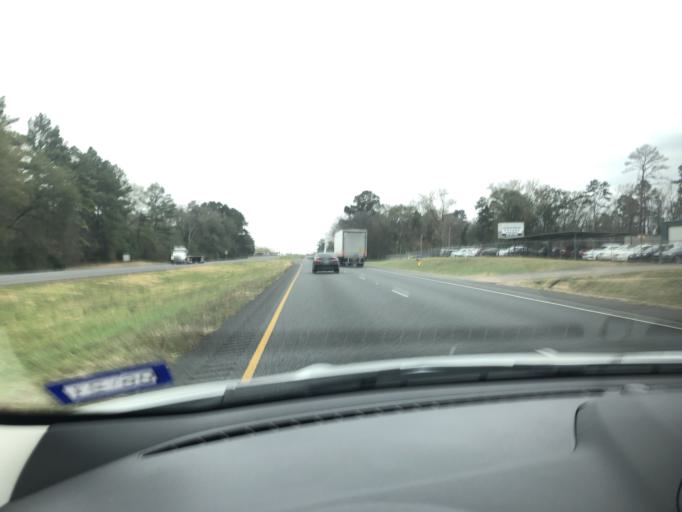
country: US
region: Texas
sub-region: Angelina County
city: Redland
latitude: 31.4704
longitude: -94.7265
